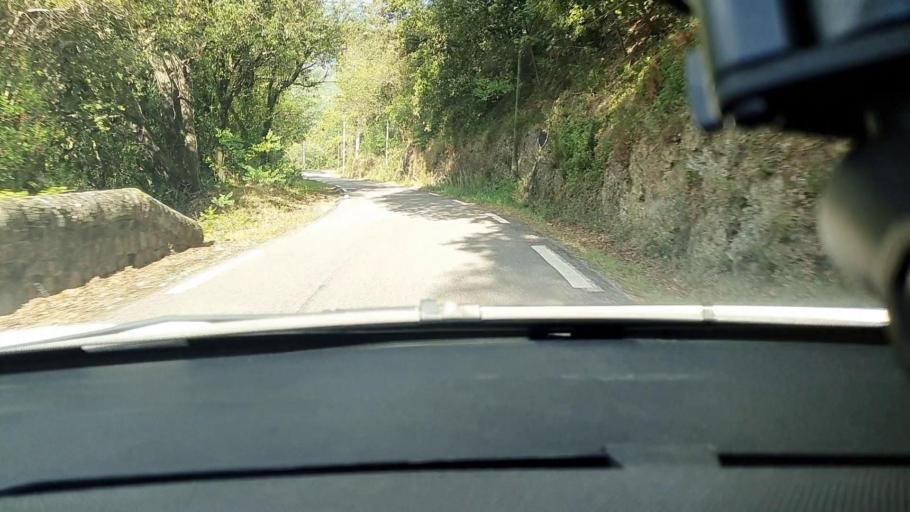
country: FR
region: Languedoc-Roussillon
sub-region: Departement du Gard
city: Besseges
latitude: 44.3646
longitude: 3.9989
